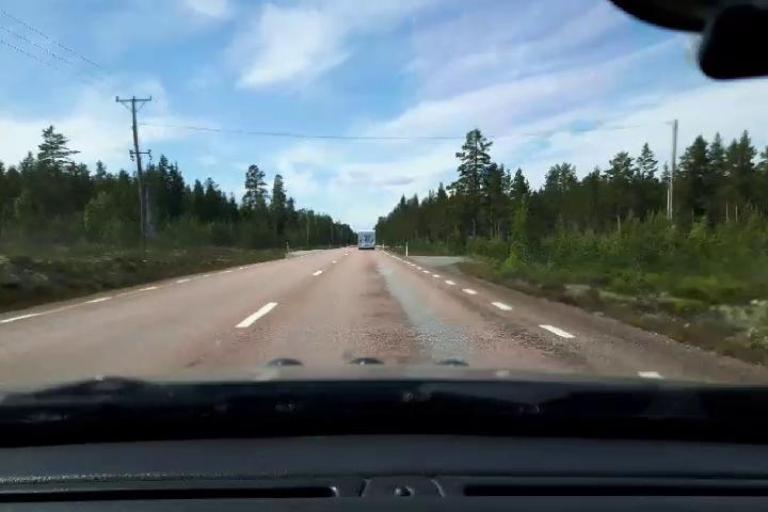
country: SE
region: Gaevleborg
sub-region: Soderhamns Kommun
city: Soderhamn
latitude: 61.1361
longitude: 16.9151
